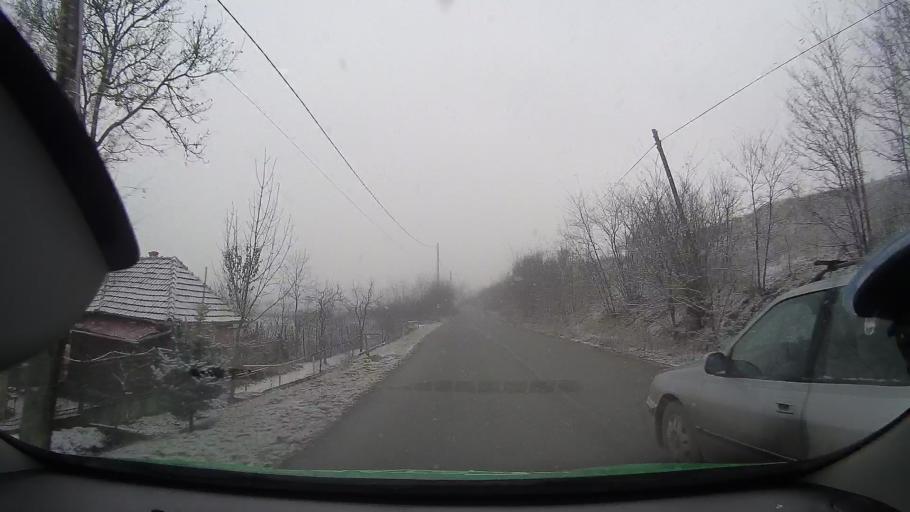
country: RO
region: Alba
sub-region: Comuna Noslac
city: Noslac
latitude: 46.3507
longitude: 23.9354
